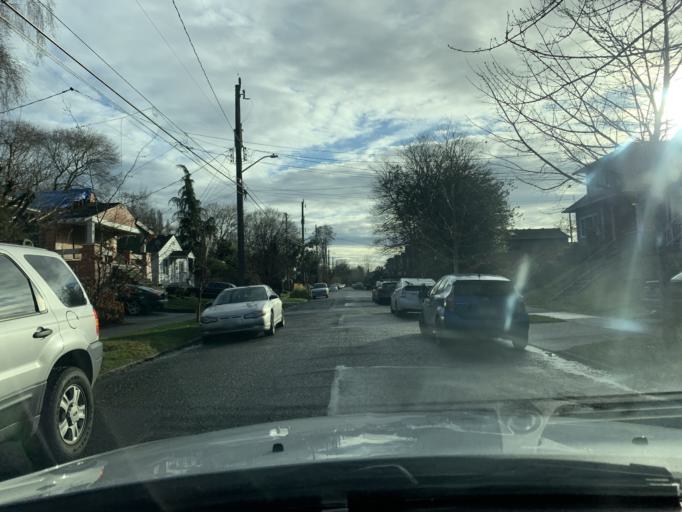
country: US
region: Washington
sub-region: King County
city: Seattle
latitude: 47.6051
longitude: -122.2979
